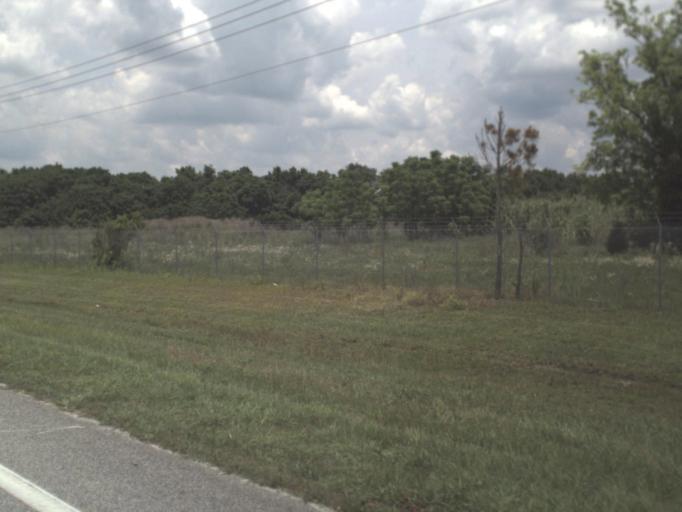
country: US
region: Florida
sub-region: Columbia County
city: Watertown
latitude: 30.1715
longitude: -82.5825
